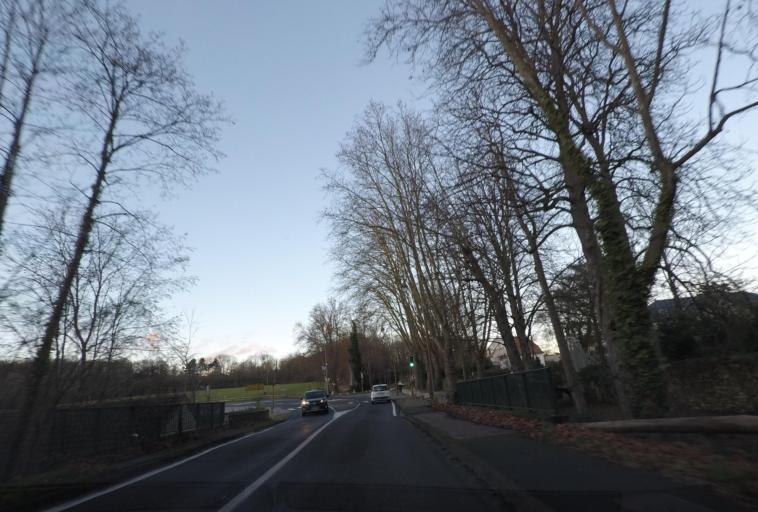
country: FR
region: Ile-de-France
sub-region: Departement de l'Essonne
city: Mennecy
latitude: 48.5779
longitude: 2.4341
